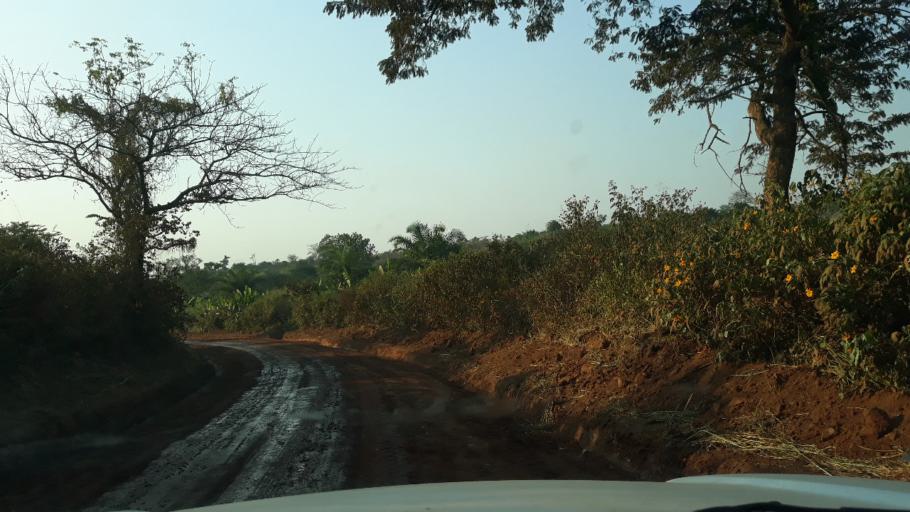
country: BI
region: Bururi
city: Rumonge
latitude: -4.2437
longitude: 28.9923
